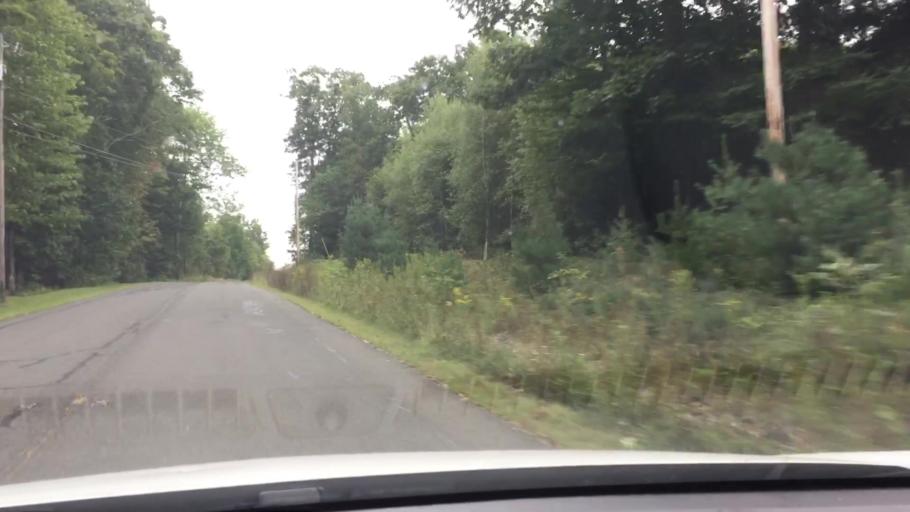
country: US
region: Massachusetts
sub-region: Berkshire County
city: Becket
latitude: 42.2581
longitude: -72.9978
